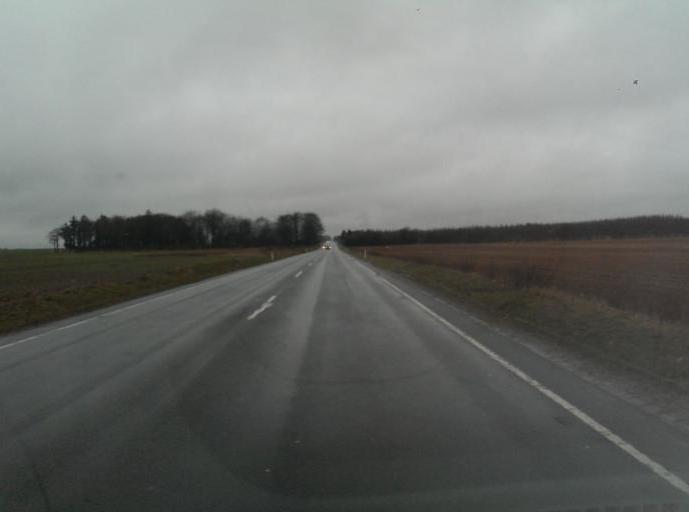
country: DK
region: South Denmark
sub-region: Varde Kommune
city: Varde
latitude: 55.6907
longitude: 8.4930
